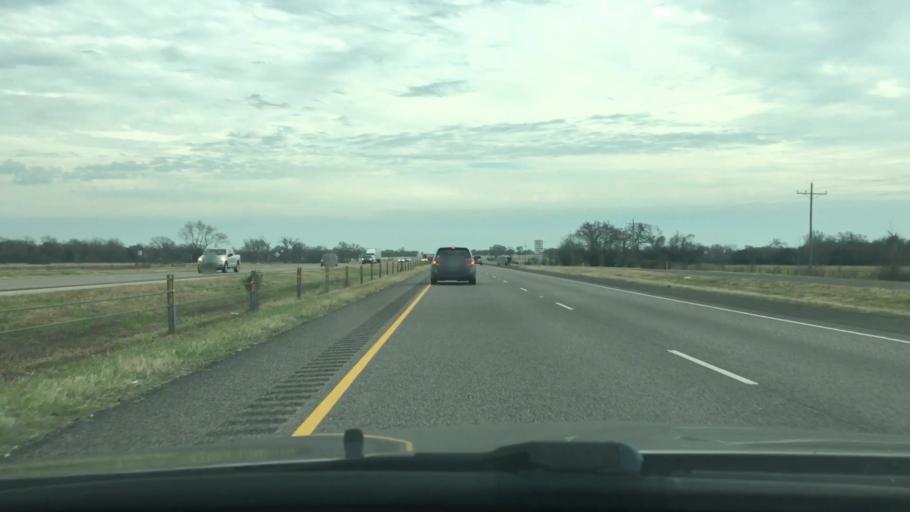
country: US
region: Texas
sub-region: Madison County
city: Madisonville
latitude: 31.0050
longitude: -95.9162
